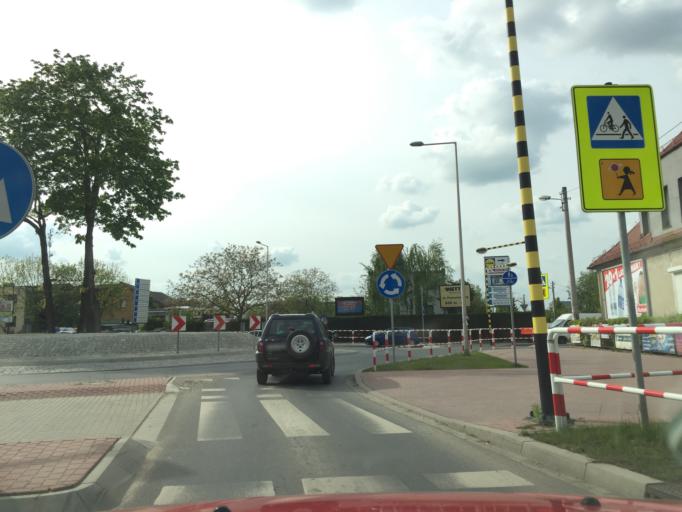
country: PL
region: Greater Poland Voivodeship
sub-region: Powiat poznanski
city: Plewiska
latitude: 52.3919
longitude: 16.7935
